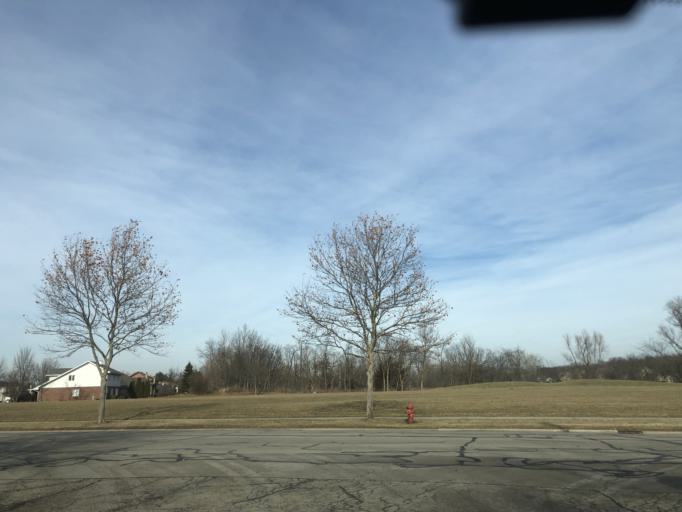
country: US
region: Illinois
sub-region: DuPage County
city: Woodridge
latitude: 41.7171
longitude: -88.0205
